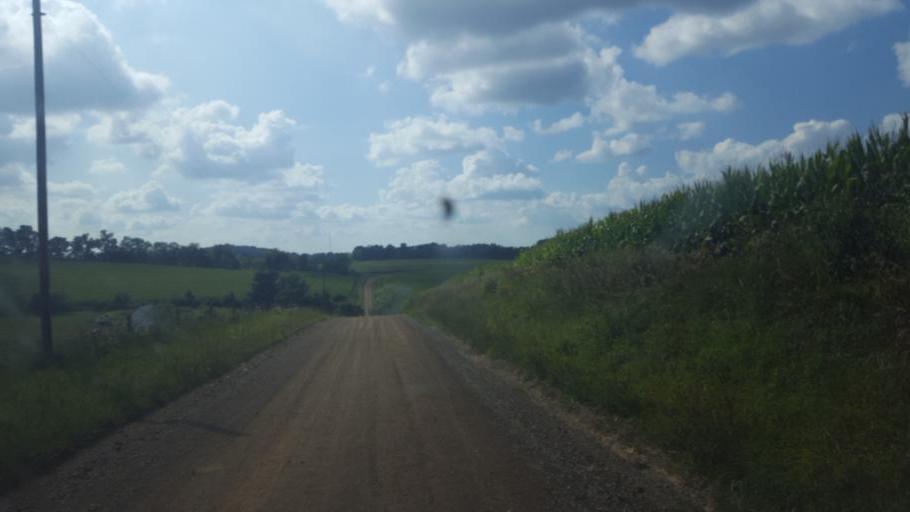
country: US
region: Ohio
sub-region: Knox County
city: Oak Hill
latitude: 40.3990
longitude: -82.2262
